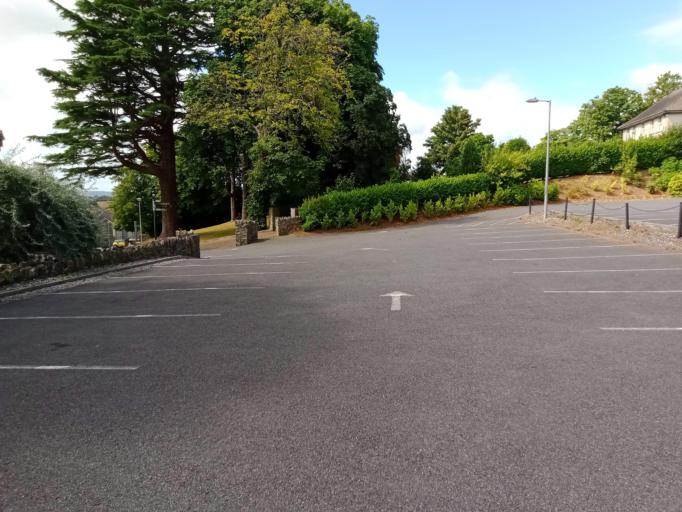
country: IE
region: Leinster
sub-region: Kilkenny
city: Thomastown
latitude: 52.5276
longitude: -7.1355
